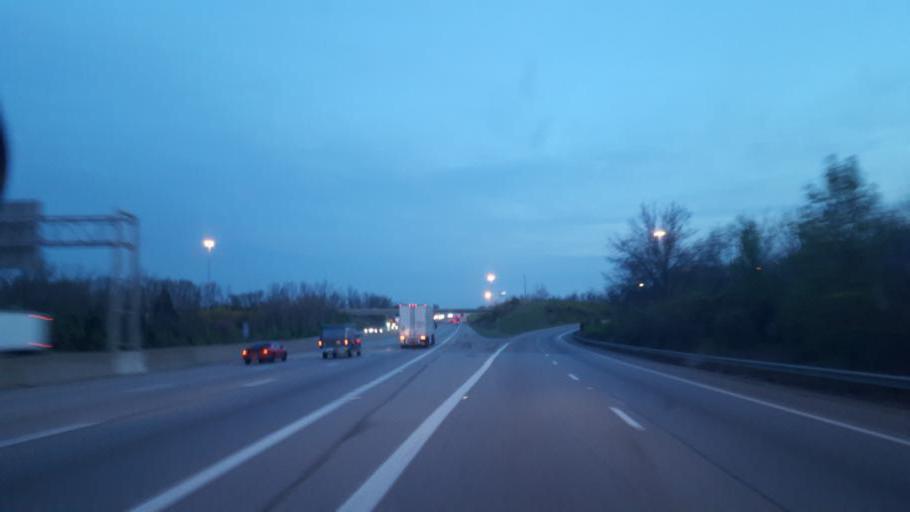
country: US
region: Kentucky
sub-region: Boone County
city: Walton
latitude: 38.8799
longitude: -84.6256
